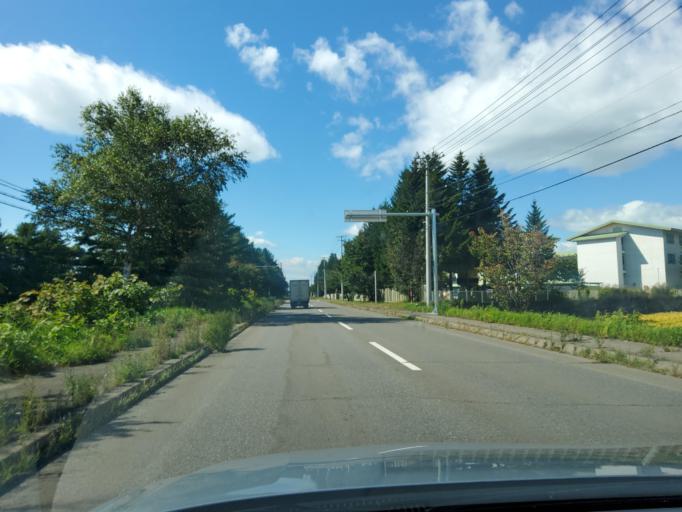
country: JP
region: Hokkaido
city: Obihiro
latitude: 42.9364
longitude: 143.2903
